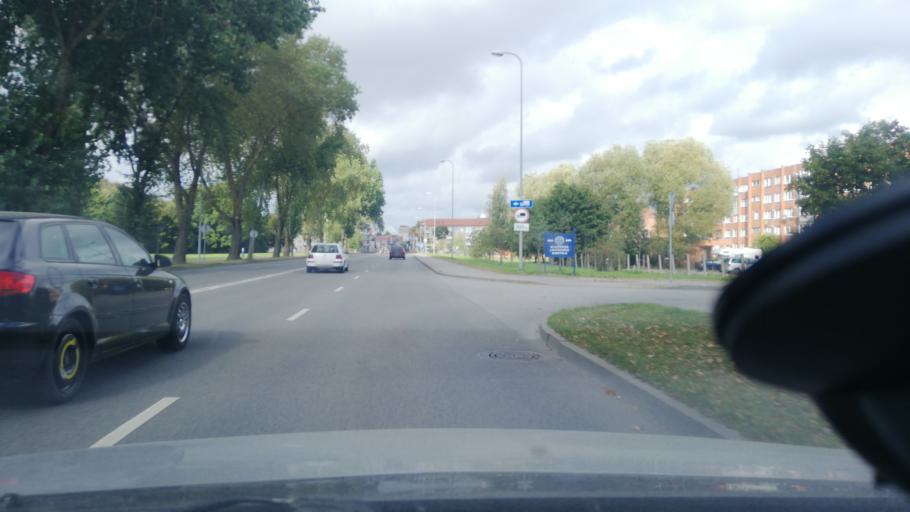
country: LT
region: Klaipedos apskritis
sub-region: Klaipeda
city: Klaipeda
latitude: 55.6732
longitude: 21.1567
